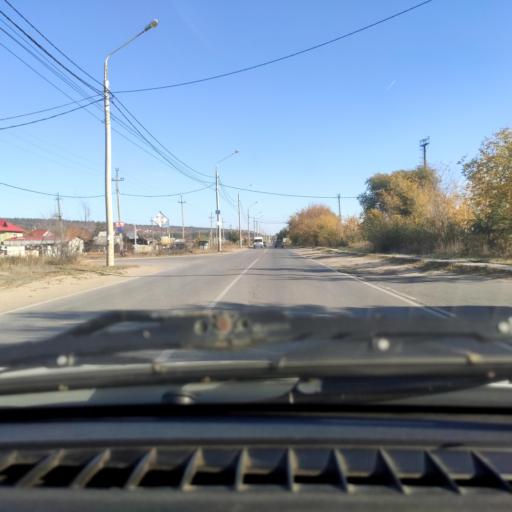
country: RU
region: Samara
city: Zhigulevsk
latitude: 53.4636
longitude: 49.5830
